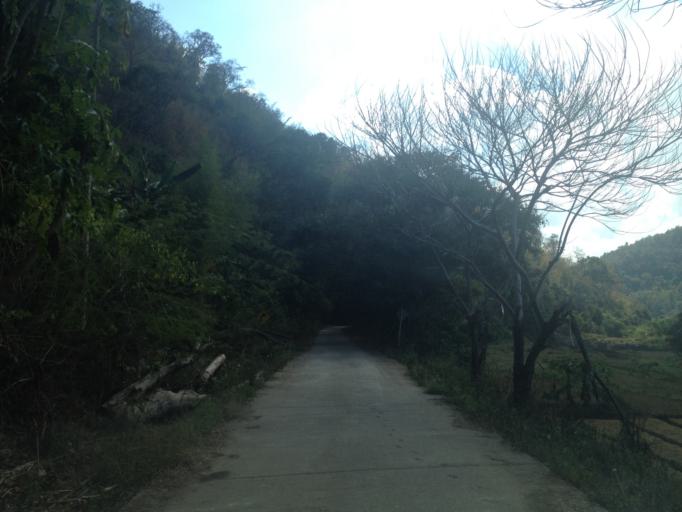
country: TH
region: Mae Hong Son
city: Ban Huai I Huak
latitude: 18.0979
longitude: 98.1895
